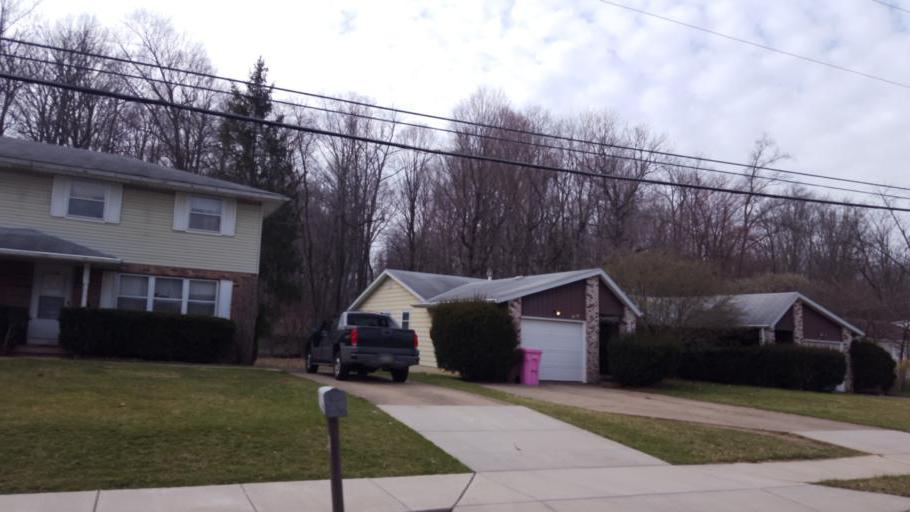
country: US
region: Ohio
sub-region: Richland County
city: Mansfield
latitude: 40.7189
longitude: -82.5389
